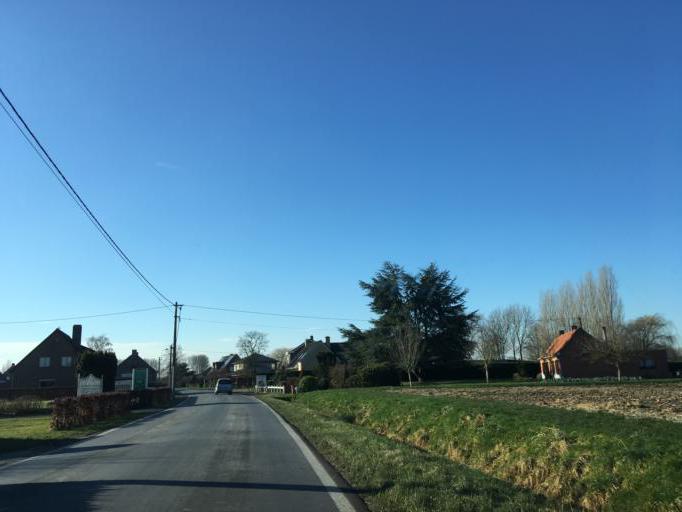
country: BE
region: Flanders
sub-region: Provincie Oost-Vlaanderen
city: Zomergem
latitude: 51.1218
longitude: 3.5881
